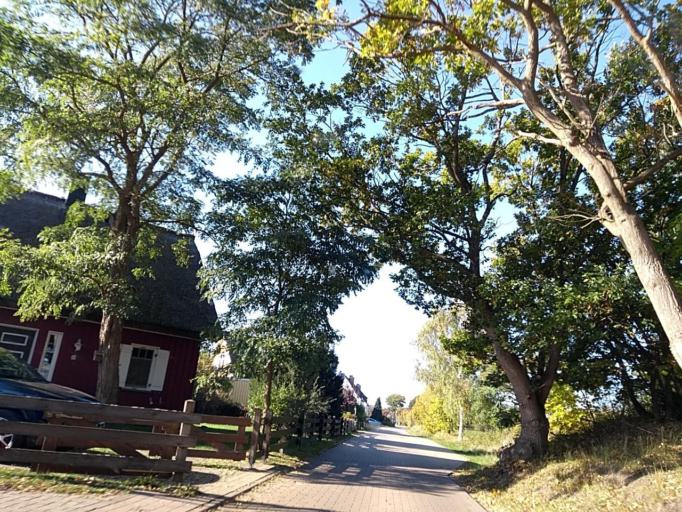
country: DE
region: Mecklenburg-Vorpommern
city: Ostseebad Prerow
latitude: 54.4111
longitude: 12.5861
